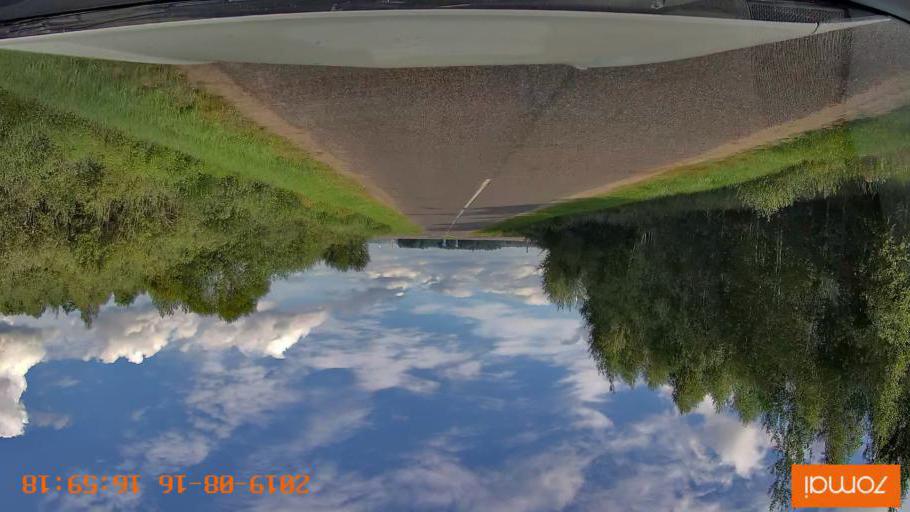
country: BY
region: Mogilev
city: Hlusha
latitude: 53.2808
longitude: 28.8409
